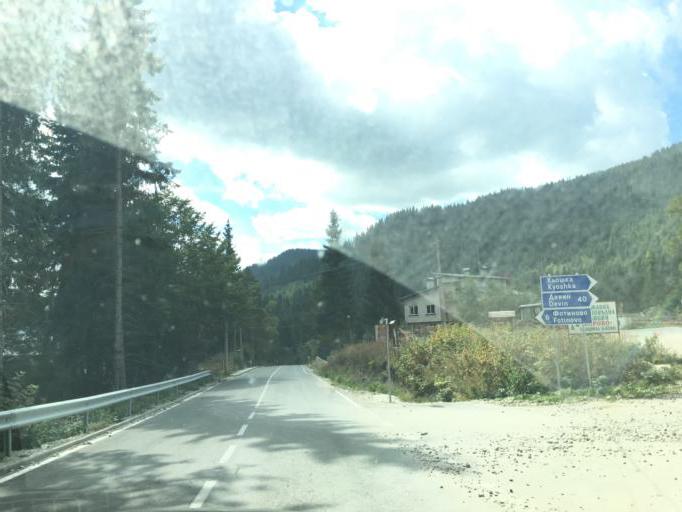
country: BG
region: Pazardzhik
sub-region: Obshtina Batak
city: Batak
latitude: 41.9073
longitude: 24.2979
